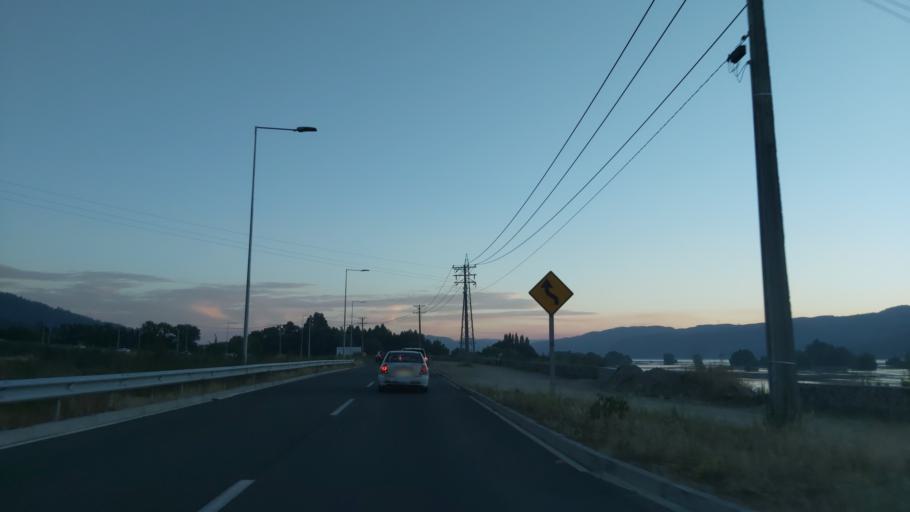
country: CL
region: Biobio
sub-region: Provincia de Concepcion
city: Chiguayante
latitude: -36.8928
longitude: -73.0366
